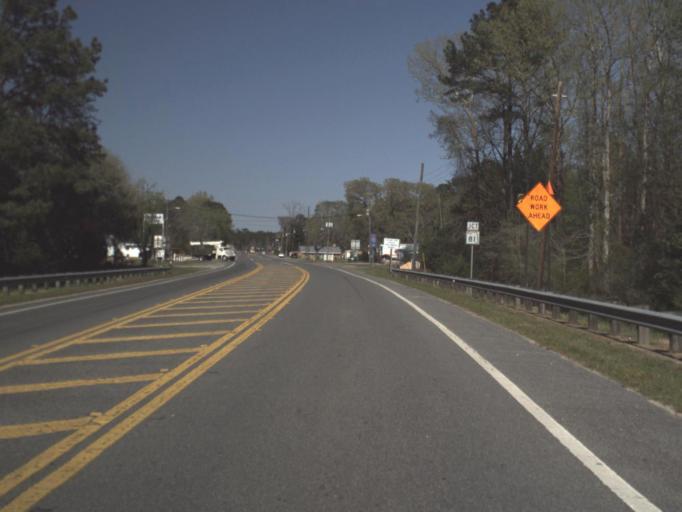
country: US
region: Florida
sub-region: Walton County
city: DeFuniak Springs
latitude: 30.7254
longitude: -85.9391
